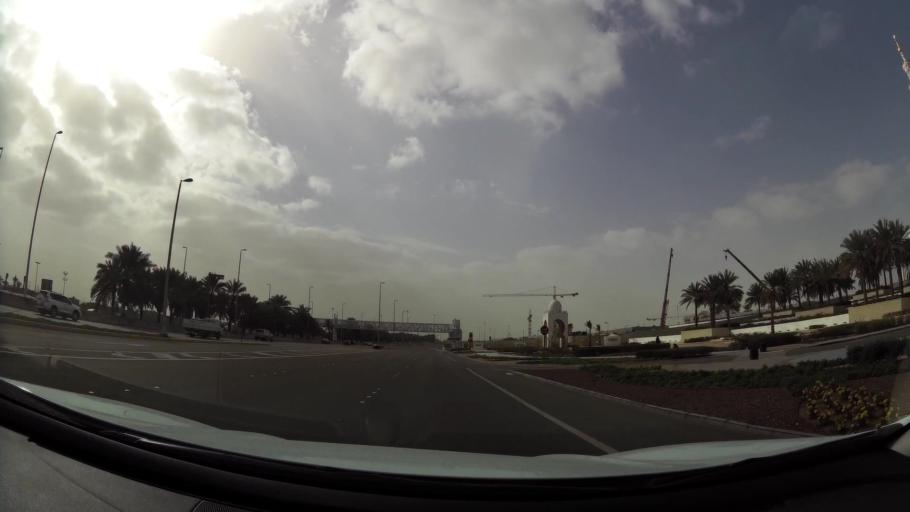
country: AE
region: Abu Dhabi
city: Abu Dhabi
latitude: 24.4125
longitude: 54.4778
